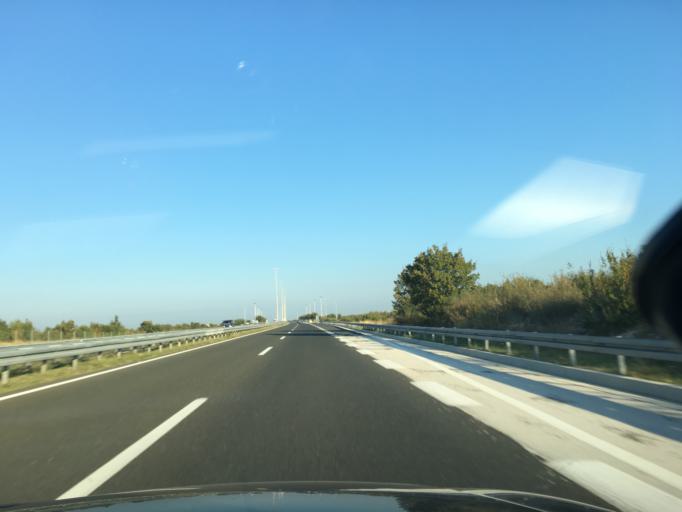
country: HR
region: Sibensko-Kniniska
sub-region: Grad Sibenik
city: Pirovac
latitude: 43.9412
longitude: 15.7006
